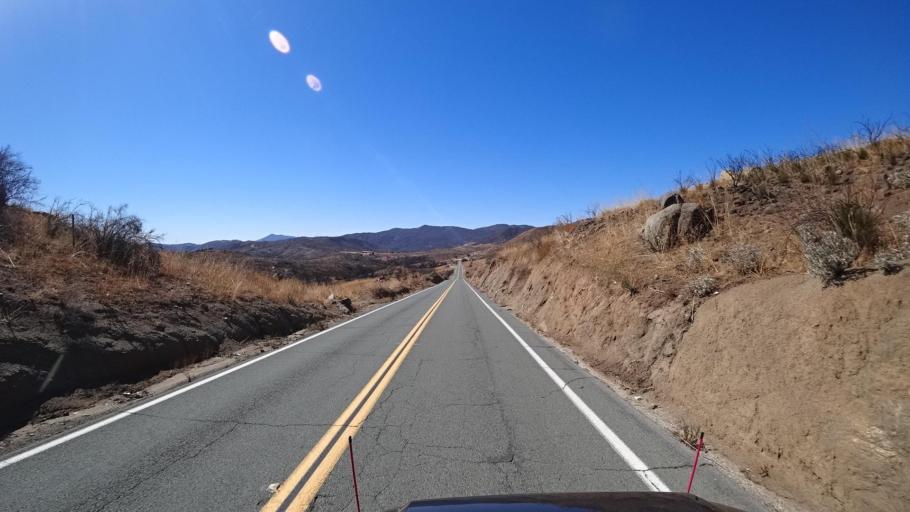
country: US
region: California
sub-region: San Diego County
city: Alpine
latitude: 32.7371
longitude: -116.6907
